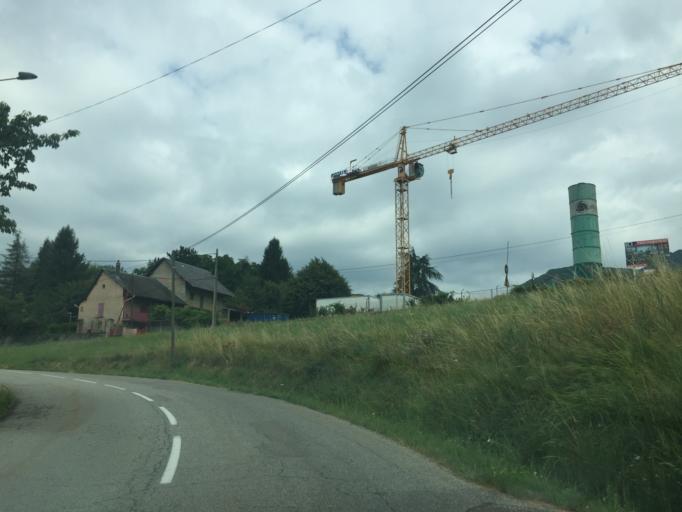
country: FR
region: Rhone-Alpes
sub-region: Departement de la Savoie
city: Barby
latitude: 45.5770
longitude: 5.9792
